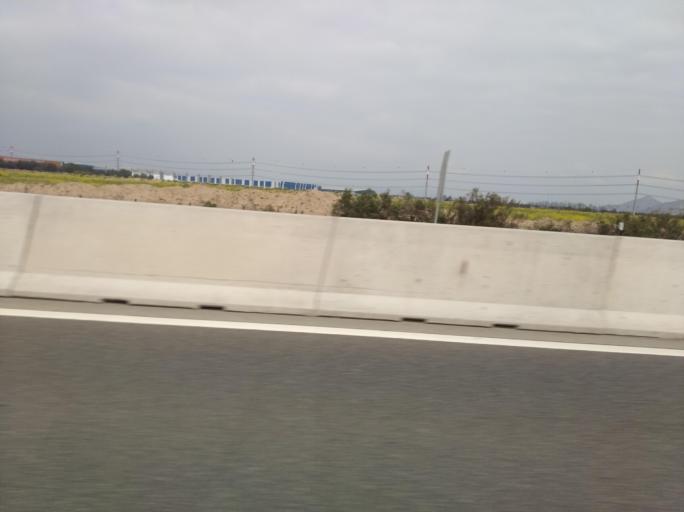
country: CL
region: Santiago Metropolitan
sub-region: Provincia de Santiago
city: Lo Prado
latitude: -33.4290
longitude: -70.8088
